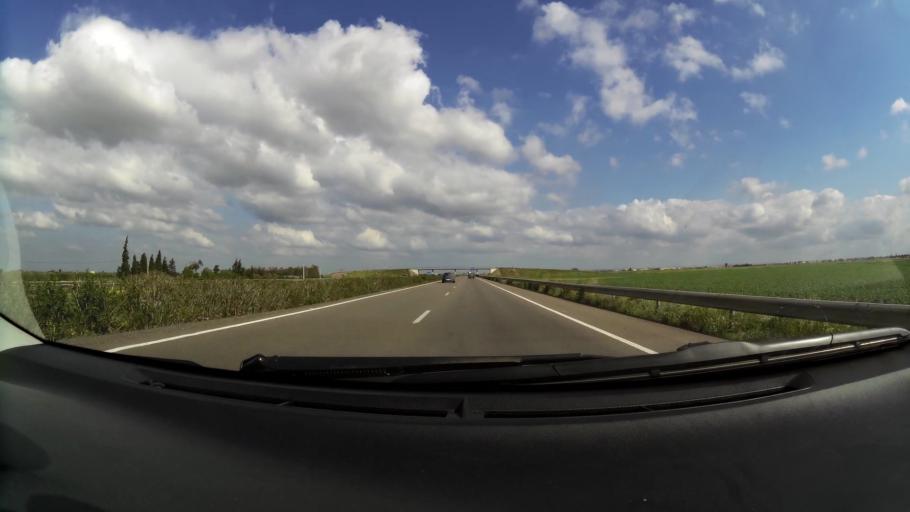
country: MA
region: Chaouia-Ouardigha
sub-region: Settat Province
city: Berrechid
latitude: 33.3080
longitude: -7.5878
